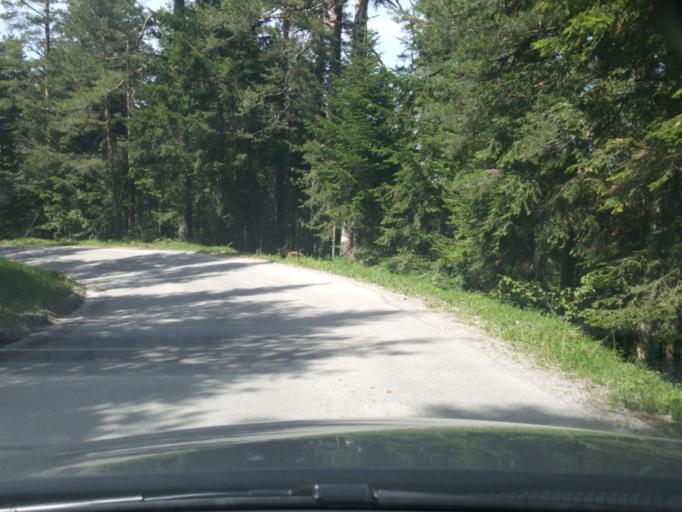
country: RS
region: Central Serbia
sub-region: Zlatiborski Okrug
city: Bajina Basta
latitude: 43.8907
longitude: 19.5328
